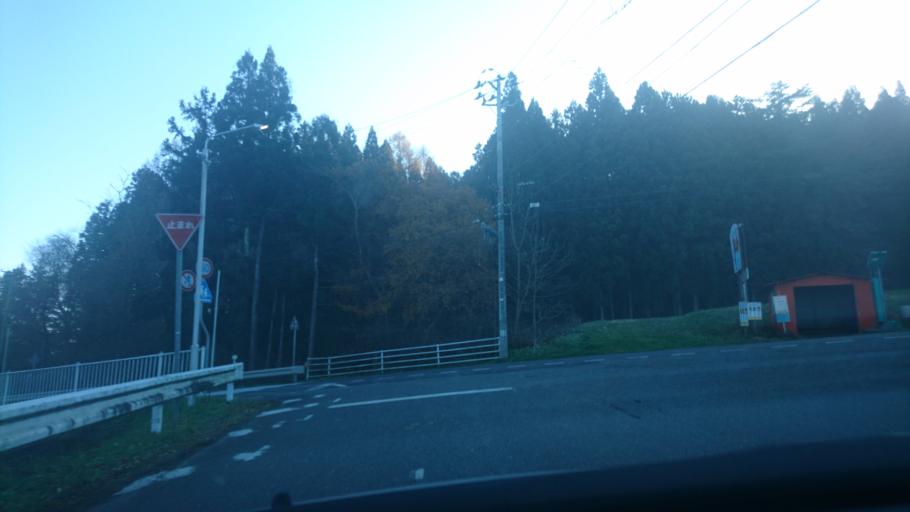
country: JP
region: Iwate
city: Ichinoseki
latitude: 38.9043
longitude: 141.2211
